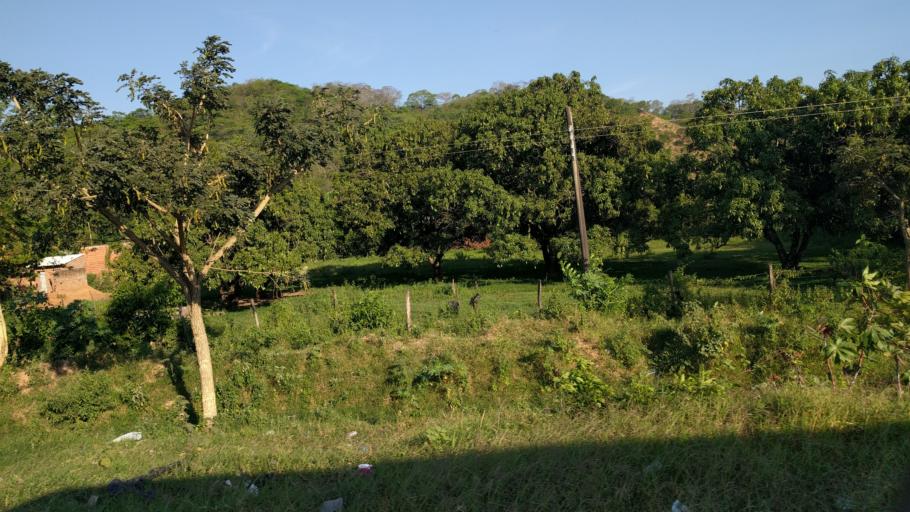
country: BO
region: Santa Cruz
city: Jorochito
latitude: -18.0589
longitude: -63.4304
